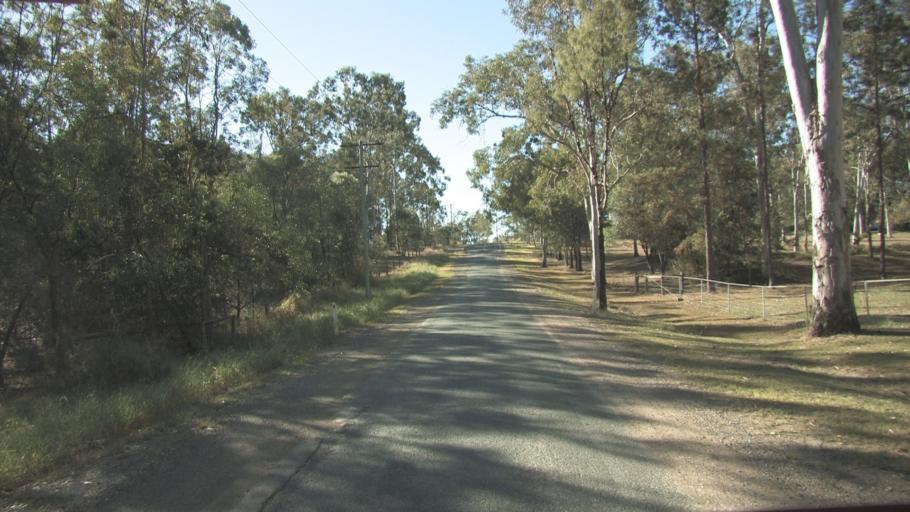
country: AU
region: Queensland
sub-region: Logan
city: North Maclean
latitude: -27.8067
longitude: 153.0339
